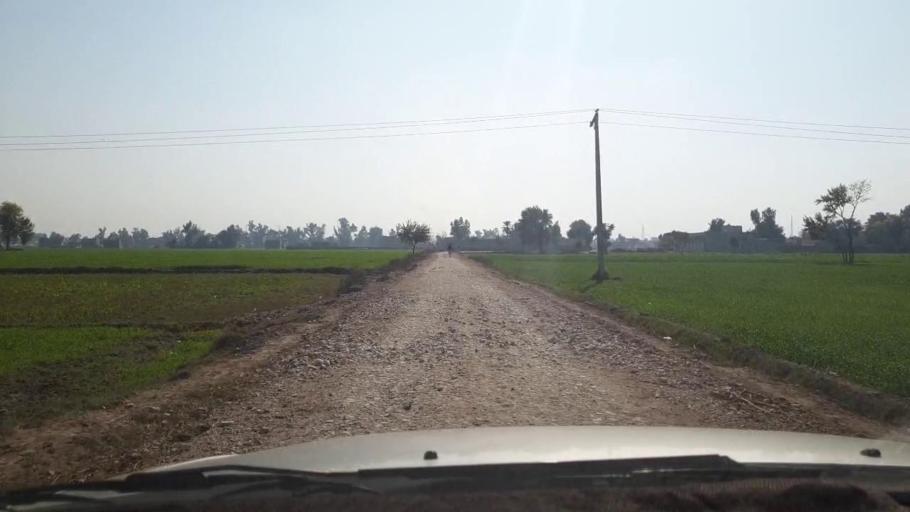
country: PK
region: Sindh
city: Mirpur Mathelo
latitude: 28.0352
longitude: 69.5517
